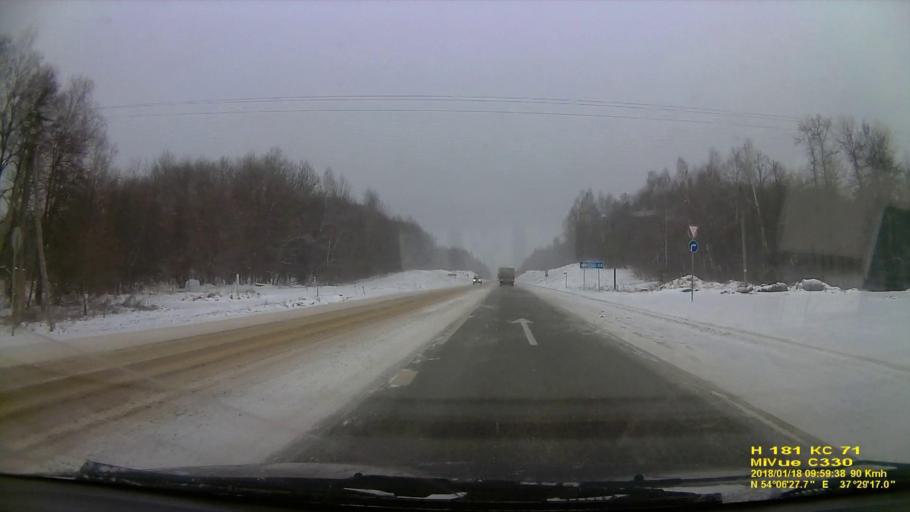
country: RU
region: Tula
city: Kosaya Gora
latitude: 54.1076
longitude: 37.4881
